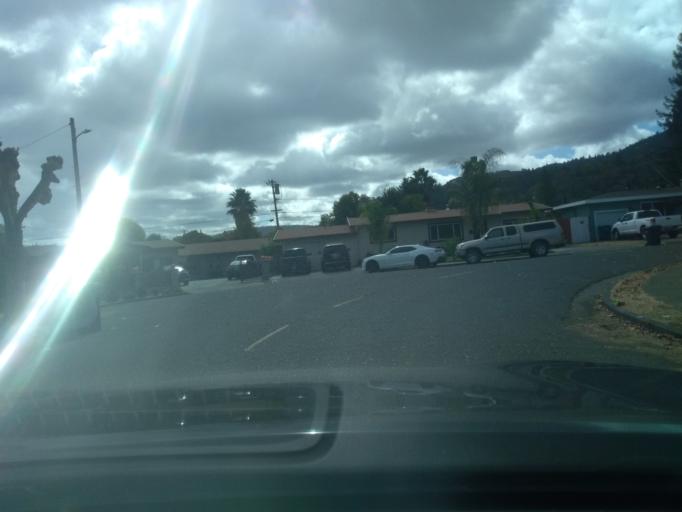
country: US
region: California
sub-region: Mendocino County
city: Ukiah
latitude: 39.1281
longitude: -123.2065
